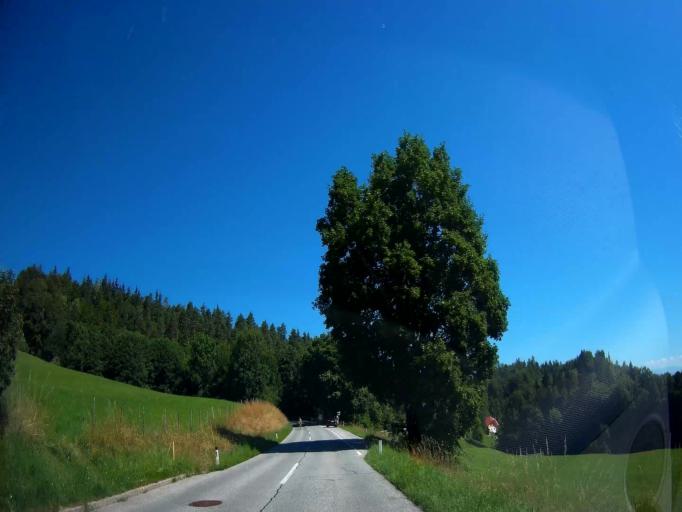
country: AT
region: Carinthia
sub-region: Politischer Bezirk Klagenfurt Land
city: Maria Worth
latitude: 46.5968
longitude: 14.1581
